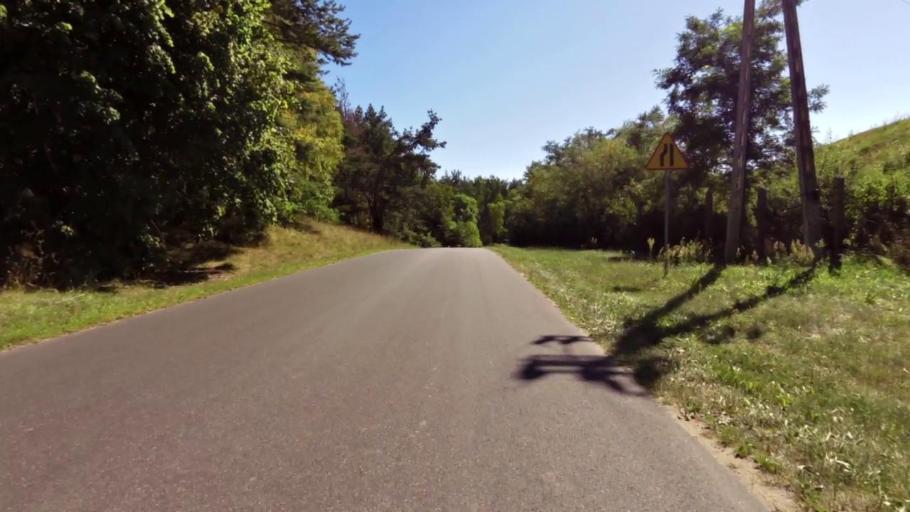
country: PL
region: West Pomeranian Voivodeship
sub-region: Powiat szczecinecki
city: Szczecinek
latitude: 53.7137
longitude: 16.6293
